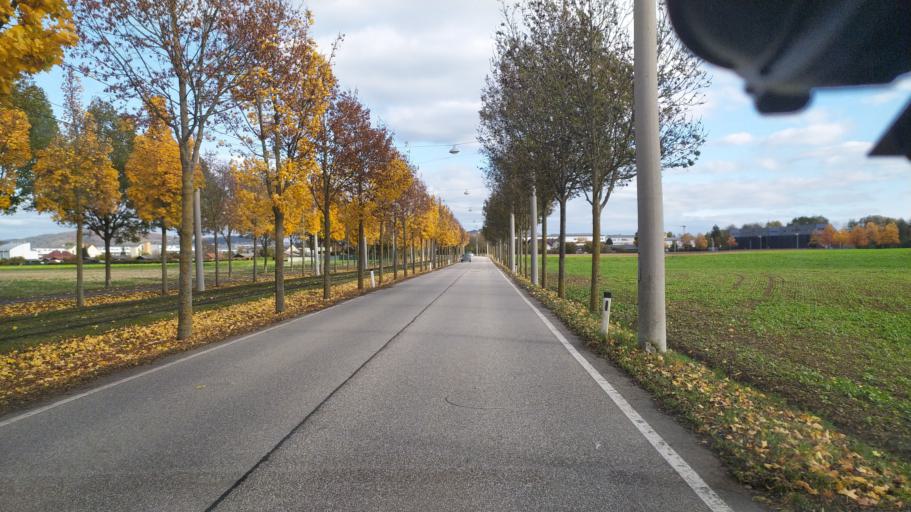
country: AT
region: Upper Austria
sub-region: Politischer Bezirk Urfahr-Umgebung
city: Steyregg
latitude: 48.2546
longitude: 14.3521
